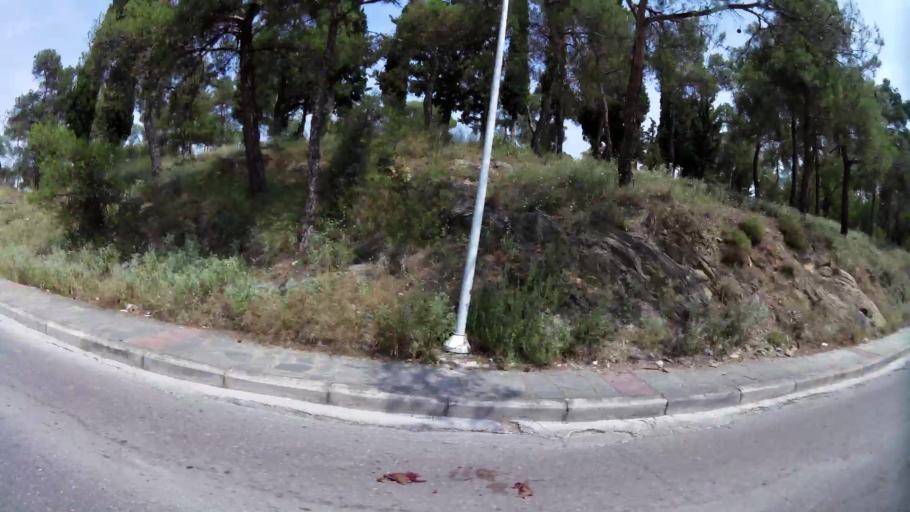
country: GR
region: Central Macedonia
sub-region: Nomos Thessalonikis
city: Agios Pavlos
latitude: 40.6349
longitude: 22.9674
